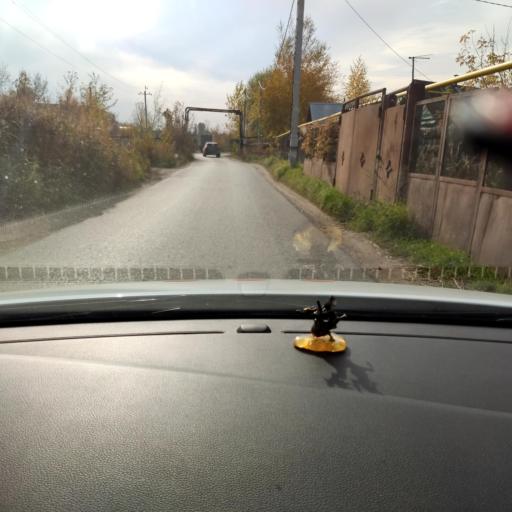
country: RU
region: Tatarstan
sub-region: Gorod Kazan'
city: Kazan
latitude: 55.7530
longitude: 49.1157
